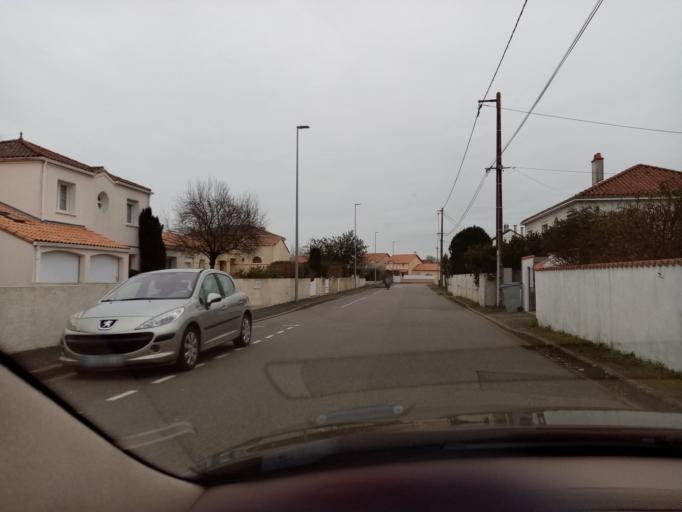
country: FR
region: Pays de la Loire
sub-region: Departement de la Loire-Atlantique
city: Saint-Sebastien-sur-Loire
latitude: 47.2007
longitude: -1.5116
